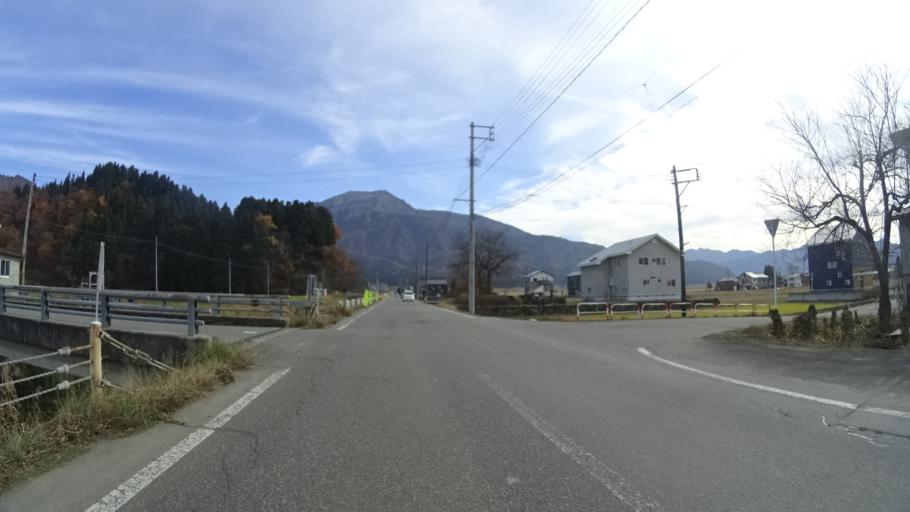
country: JP
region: Niigata
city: Muikamachi
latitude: 37.0473
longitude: 138.8820
